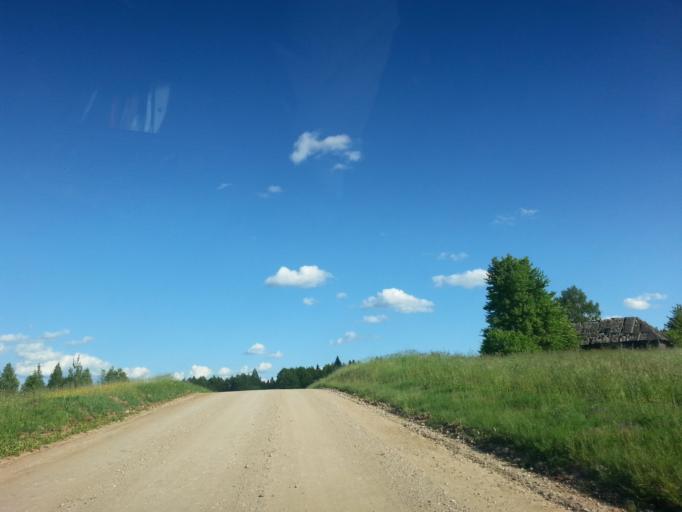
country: BY
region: Minsk
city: Narach
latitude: 54.9768
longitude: 26.6218
